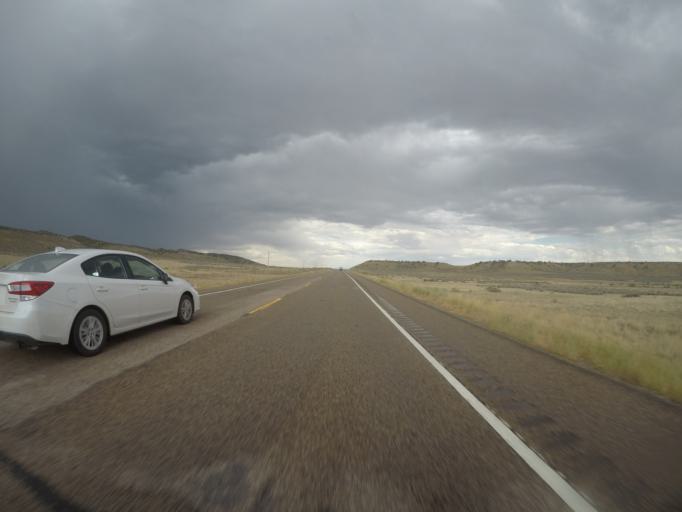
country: US
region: Colorado
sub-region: Rio Blanco County
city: Rangely
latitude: 40.2414
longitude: -108.9386
